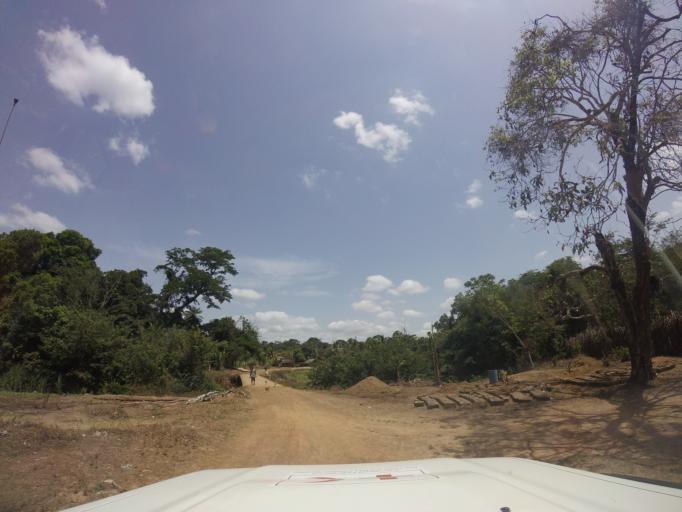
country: SL
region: Southern Province
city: Zimmi
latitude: 7.1344
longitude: -11.2840
